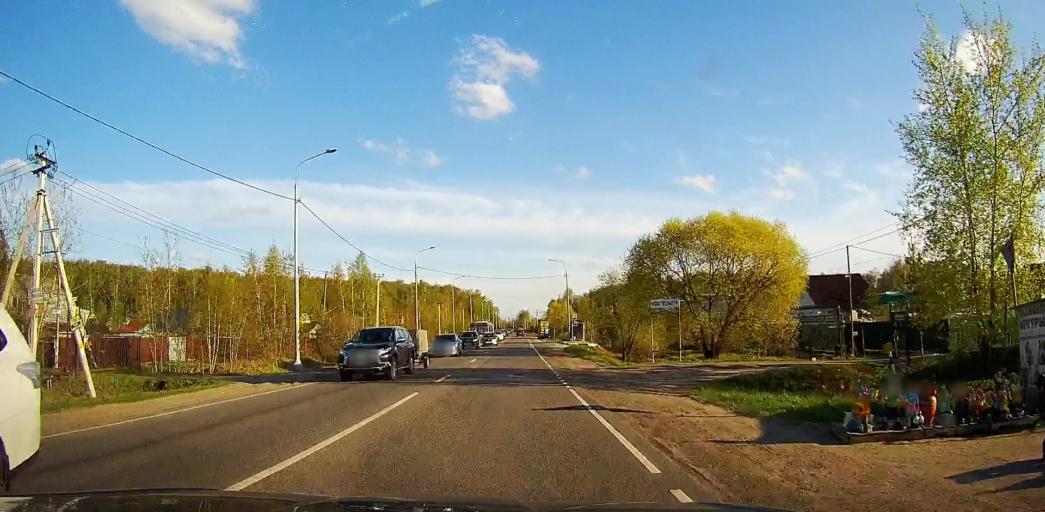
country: RU
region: Moskovskaya
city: Bronnitsy
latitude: 55.3837
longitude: 38.2071
